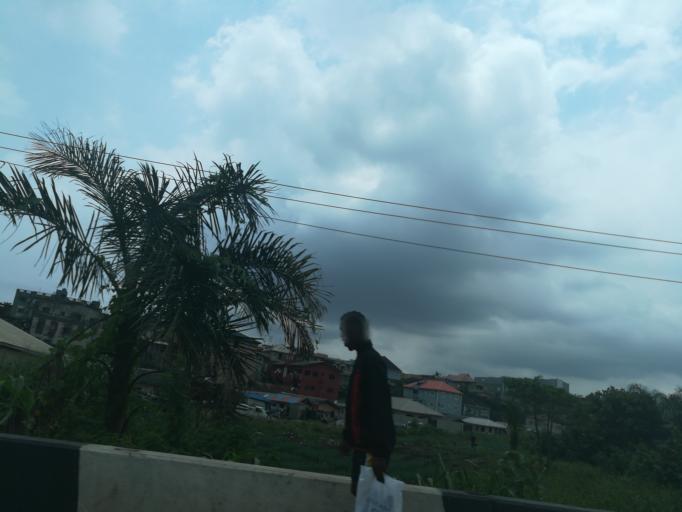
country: NG
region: Lagos
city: Ojota
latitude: 6.5776
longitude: 3.3960
